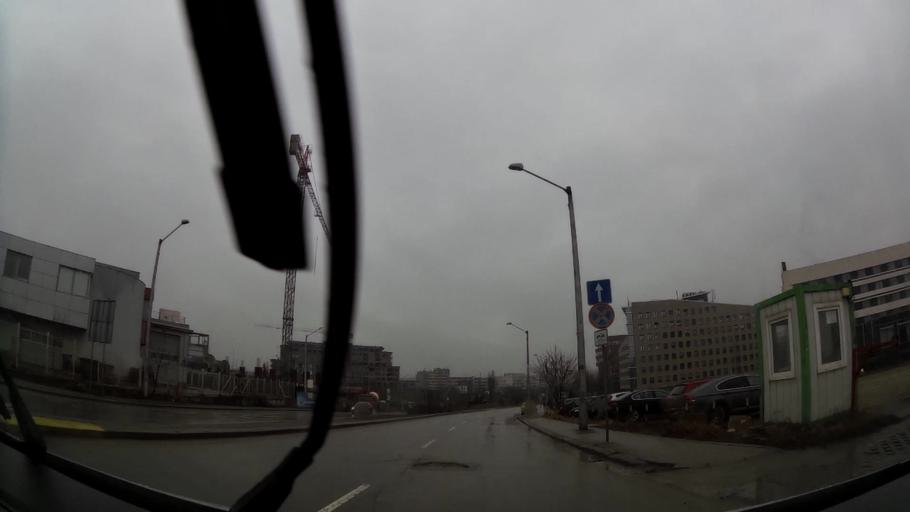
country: BG
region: Sofia-Capital
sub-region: Stolichna Obshtina
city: Sofia
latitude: 42.6243
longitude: 23.3748
